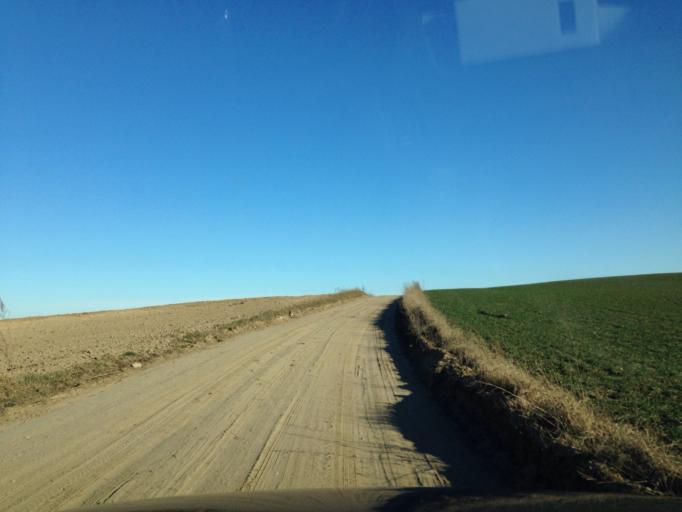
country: PL
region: Kujawsko-Pomorskie
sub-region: Powiat brodnicki
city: Brzozie
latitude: 53.3426
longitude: 19.6481
